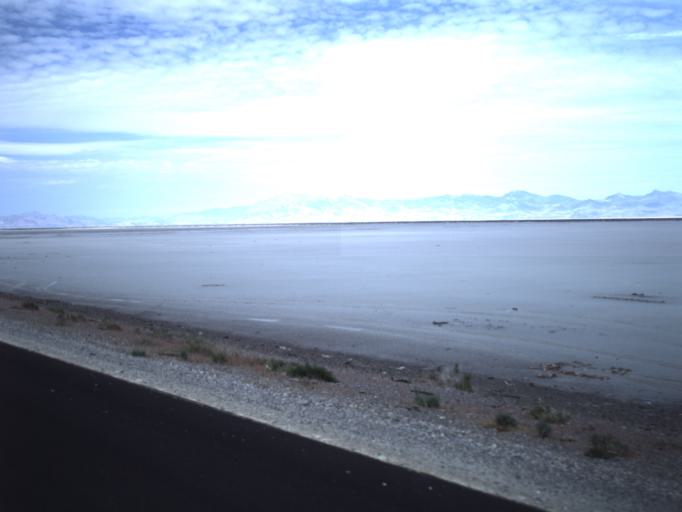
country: US
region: Utah
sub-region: Tooele County
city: Wendover
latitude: 40.7329
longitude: -113.5469
